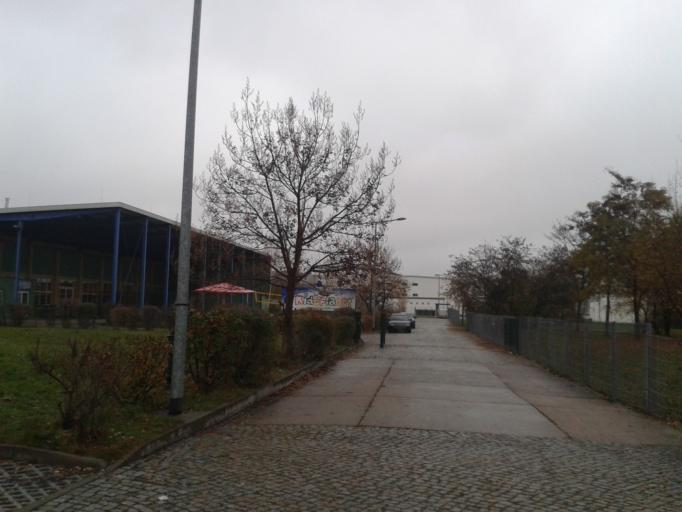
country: DE
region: Saxony
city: Heidenau
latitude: 51.0052
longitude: 13.8306
